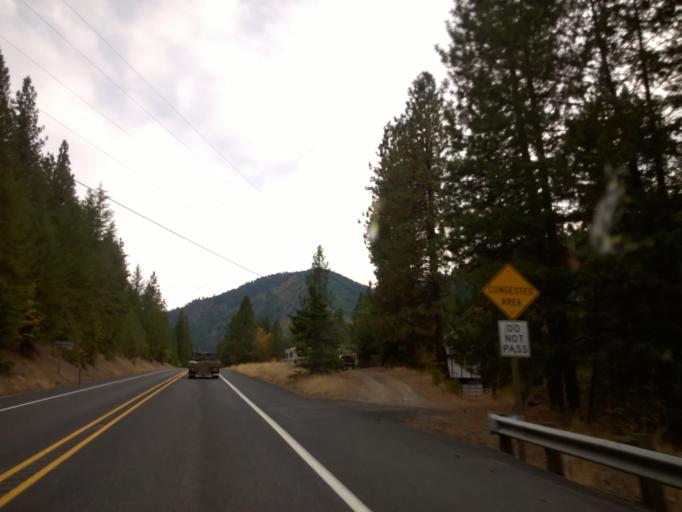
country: US
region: Washington
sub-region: Chelan County
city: Leavenworth
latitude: 47.4822
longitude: -120.6531
